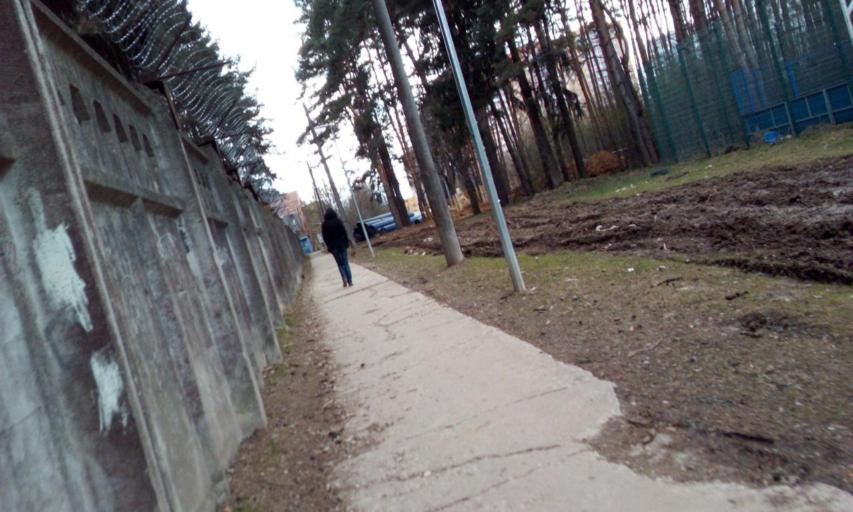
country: RU
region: Moskovskaya
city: Troitsk
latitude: 55.4871
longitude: 37.3138
